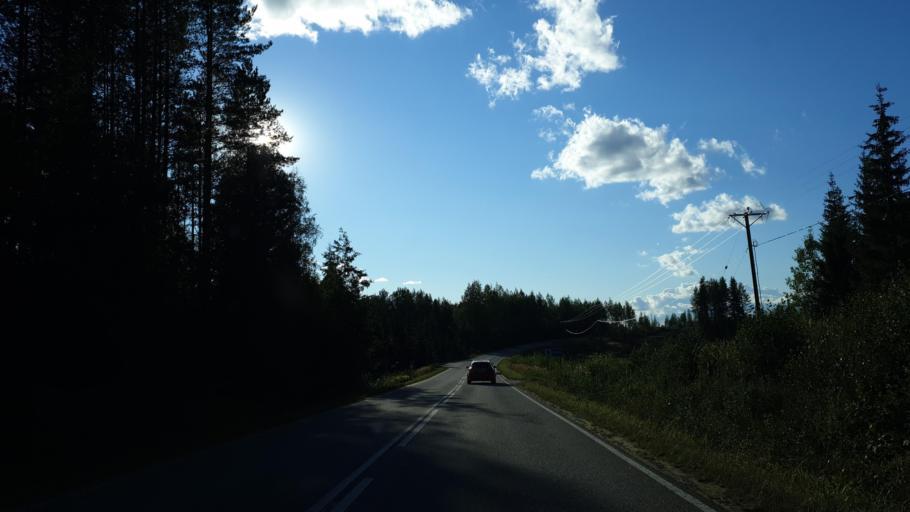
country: FI
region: Northern Savo
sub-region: Koillis-Savo
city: Kaavi
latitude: 62.9997
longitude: 28.4305
